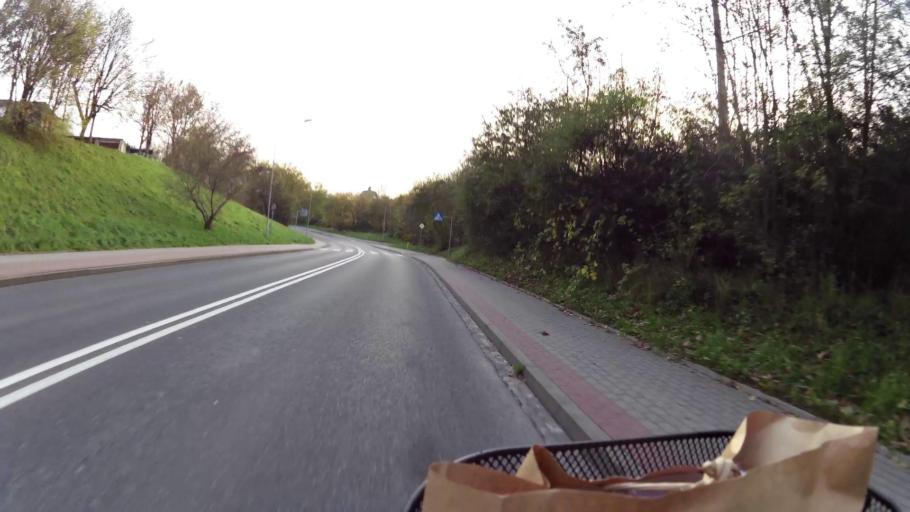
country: PL
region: West Pomeranian Voivodeship
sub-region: Koszalin
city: Koszalin
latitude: 54.2034
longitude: 16.1745
